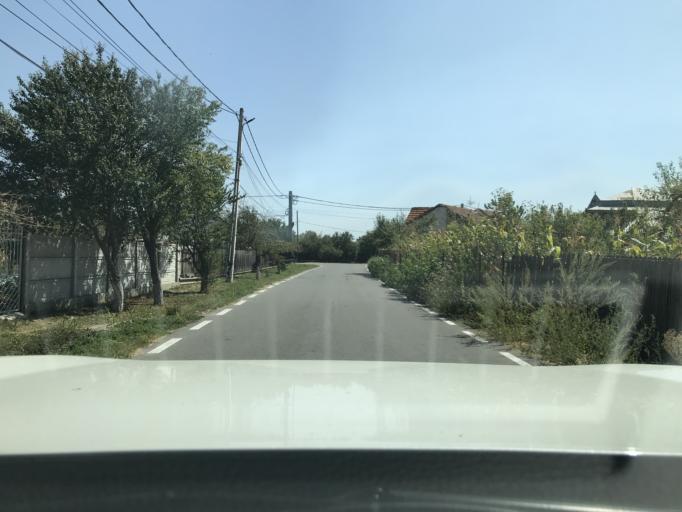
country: RO
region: Olt
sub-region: Comuna Falcoiu
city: Falcoiu
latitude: 44.2439
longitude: 24.3662
